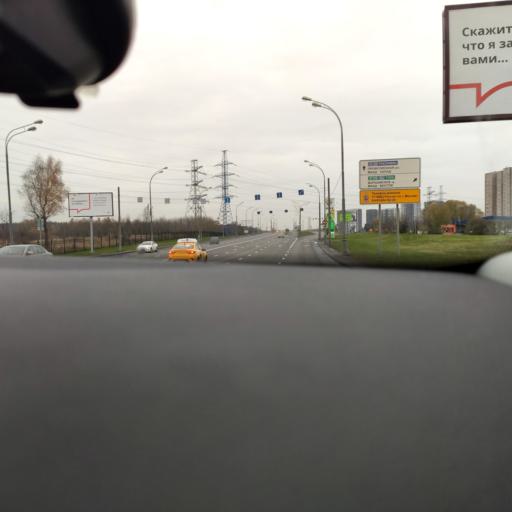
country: RU
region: Moscow
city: Chertanovo Yuzhnoye
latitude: 55.5767
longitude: 37.5651
